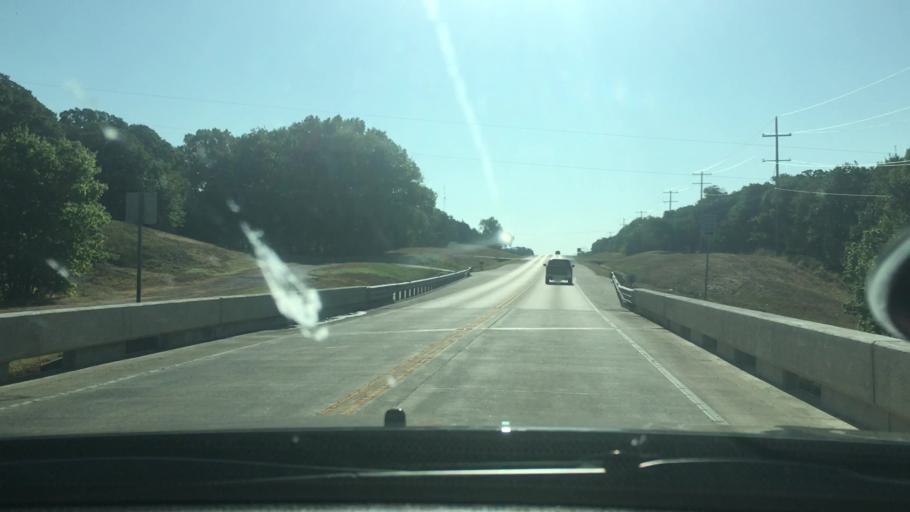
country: US
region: Oklahoma
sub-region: Johnston County
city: Tishomingo
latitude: 34.2369
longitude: -96.7171
